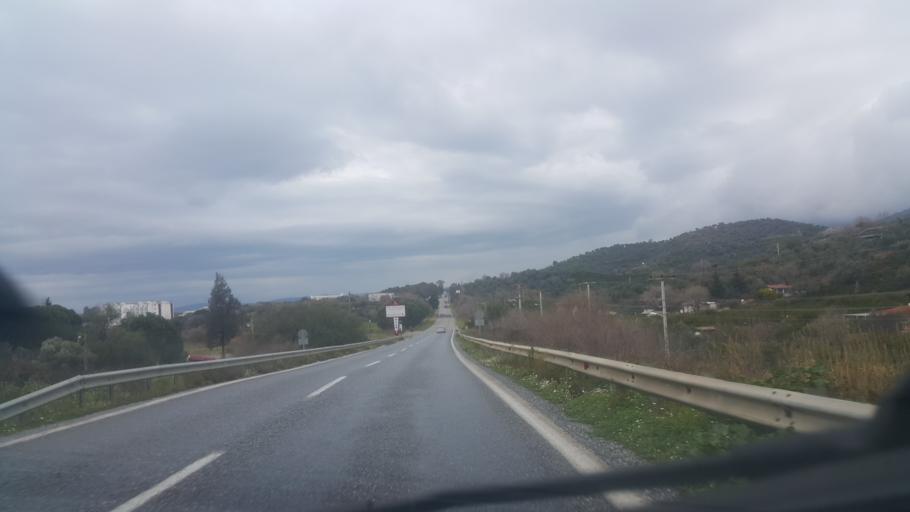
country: TR
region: Izmir
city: Ozdere
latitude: 37.9916
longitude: 27.1380
